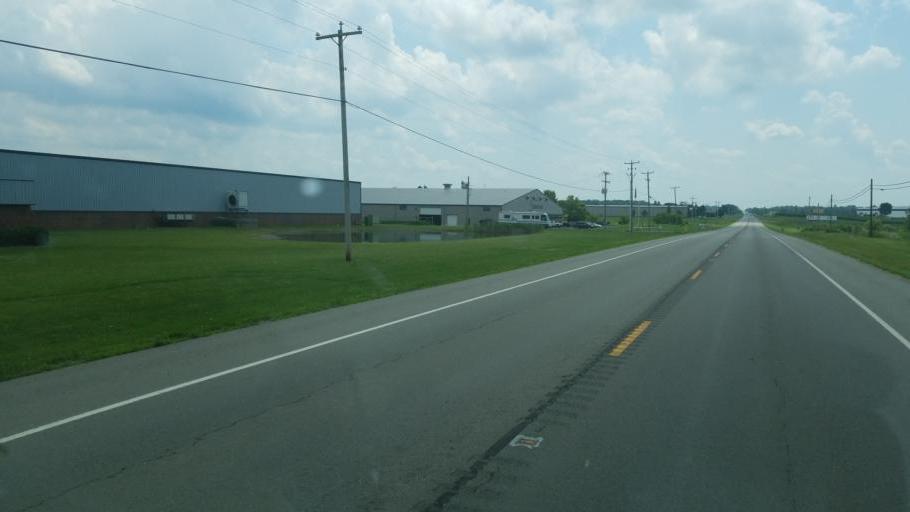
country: US
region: Ohio
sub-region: Hardin County
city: Kenton
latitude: 40.6208
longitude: -83.6227
